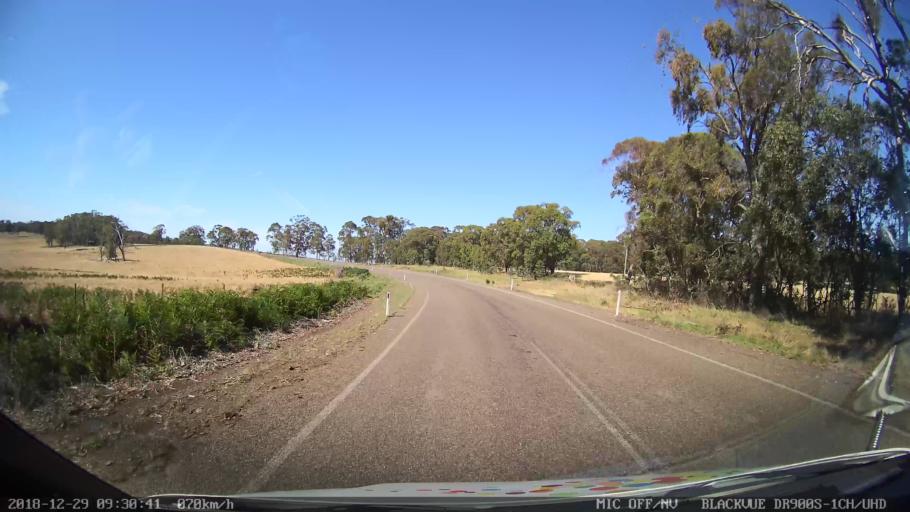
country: AU
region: New South Wales
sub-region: Upper Lachlan Shire
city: Crookwell
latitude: -34.6005
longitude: 149.3670
